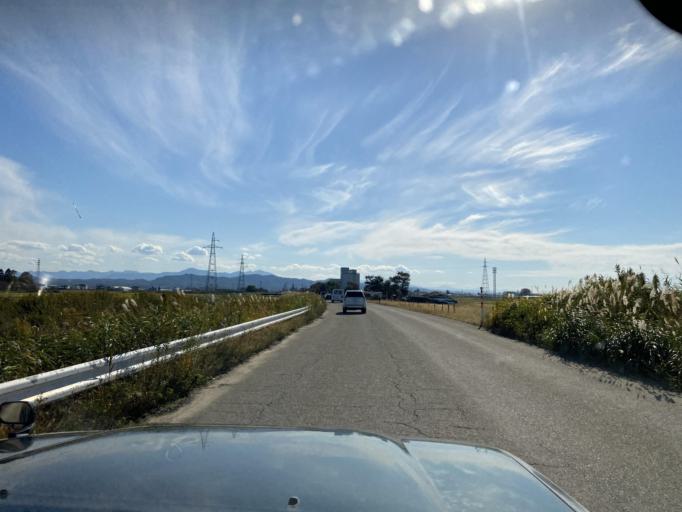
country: JP
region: Niigata
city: Niitsu-honcho
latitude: 37.7996
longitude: 139.0768
